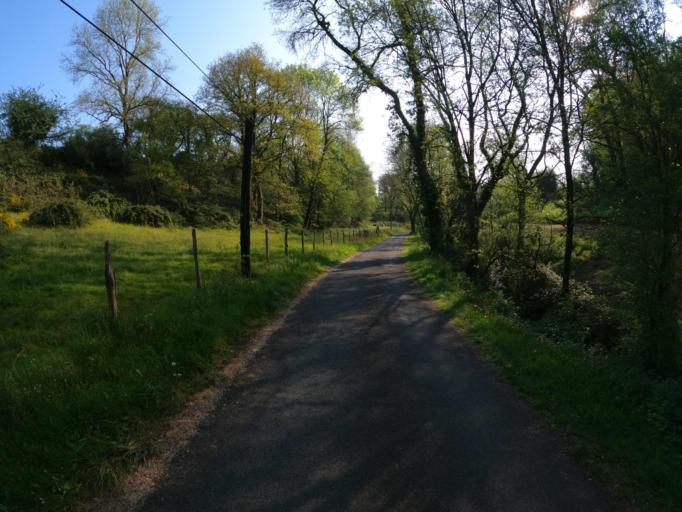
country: FR
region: Pays de la Loire
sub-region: Departement de Maine-et-Loire
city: La Romagne
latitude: 47.0654
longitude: -1.0122
